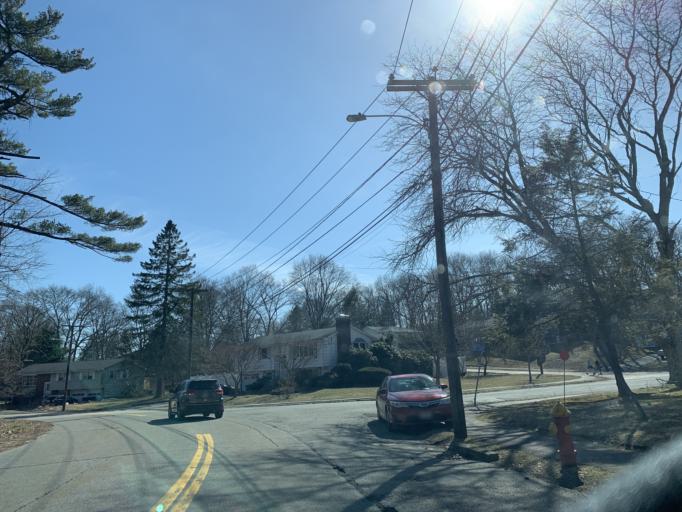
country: US
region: Massachusetts
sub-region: Norfolk County
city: Westwood
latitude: 42.1901
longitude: -71.2245
